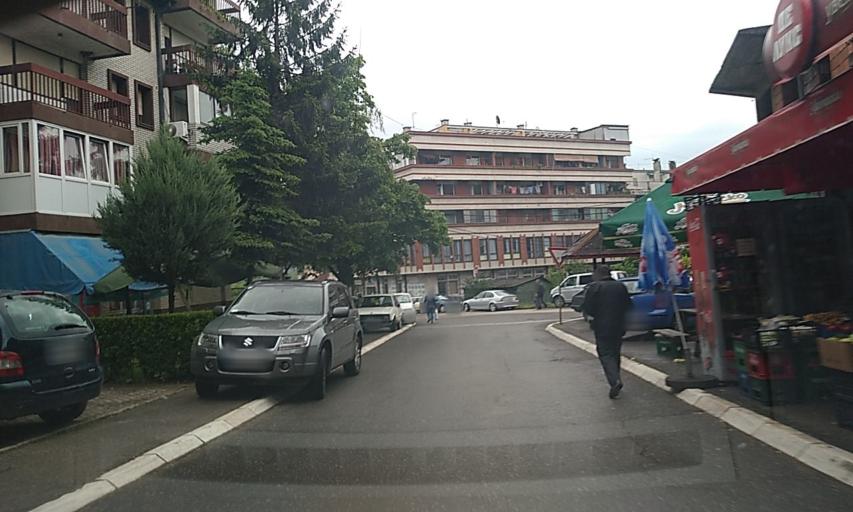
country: RS
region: Central Serbia
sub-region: Pcinjski Okrug
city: Vladicin Han
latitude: 42.7085
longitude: 22.0574
